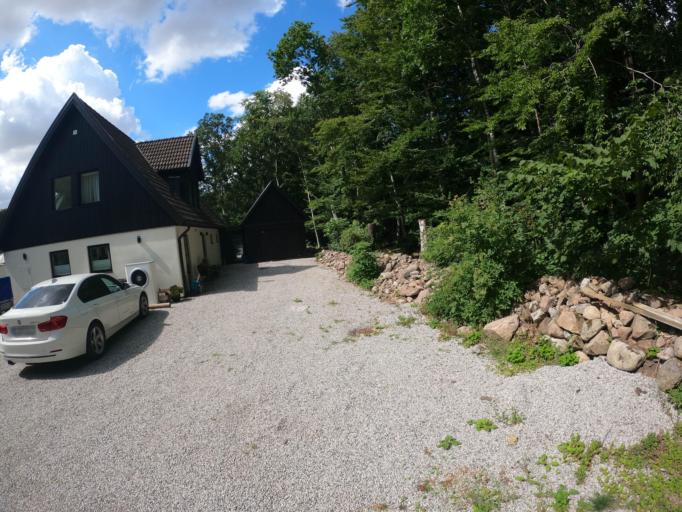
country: SE
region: Skane
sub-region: Lunds Kommun
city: Genarp
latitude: 55.6776
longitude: 13.3611
